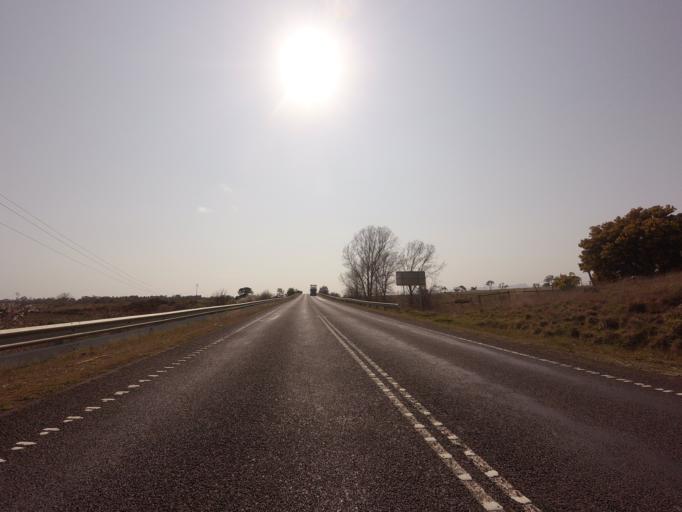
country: AU
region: Tasmania
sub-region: Northern Midlands
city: Evandale
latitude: -41.8429
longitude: 147.4481
